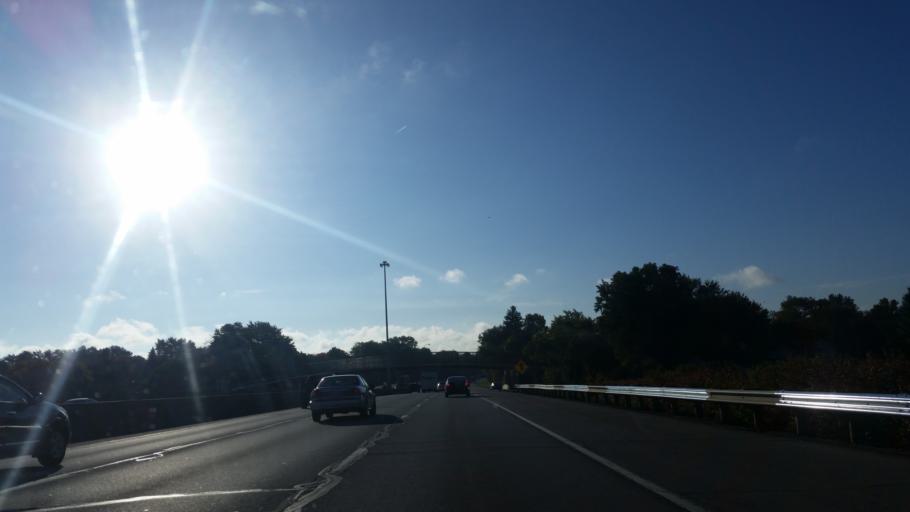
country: US
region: Ohio
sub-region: Summit County
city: Fairlawn
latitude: 41.0831
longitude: -81.5784
